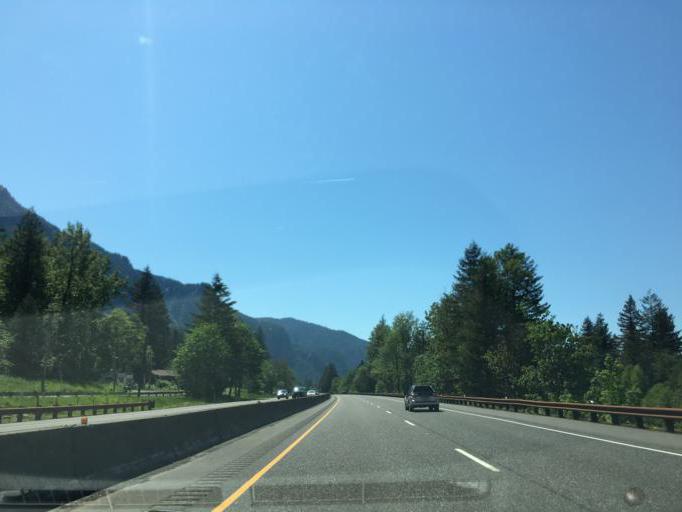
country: US
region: Oregon
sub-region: Hood River County
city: Cascade Locks
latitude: 45.6074
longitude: -122.0341
